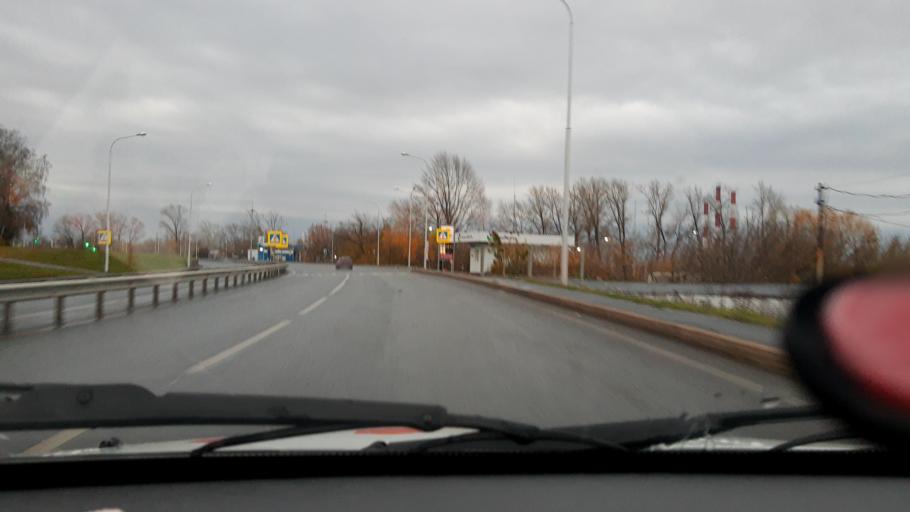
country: RU
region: Bashkortostan
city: Ufa
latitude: 54.8023
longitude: 56.1129
